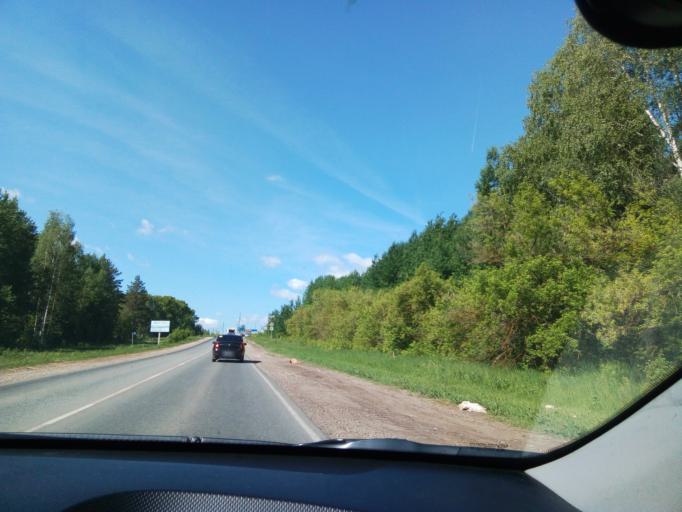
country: RU
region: Chuvashia
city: Novocheboksarsk
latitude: 56.0791
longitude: 47.4993
